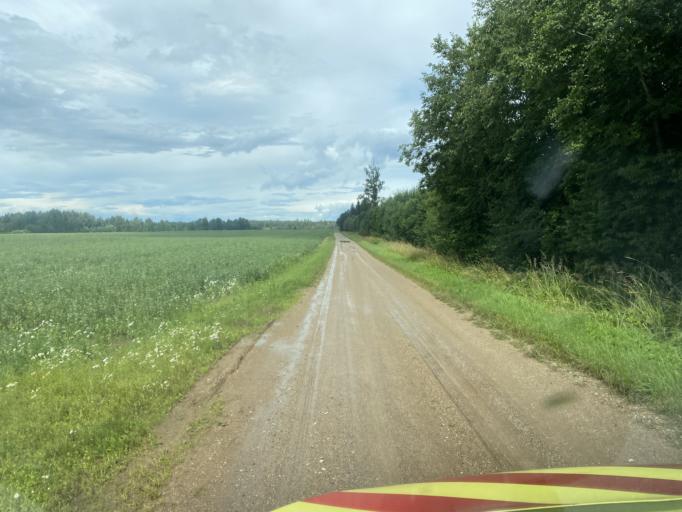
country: EE
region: Valgamaa
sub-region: Torva linn
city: Torva
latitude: 58.0996
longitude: 26.0023
